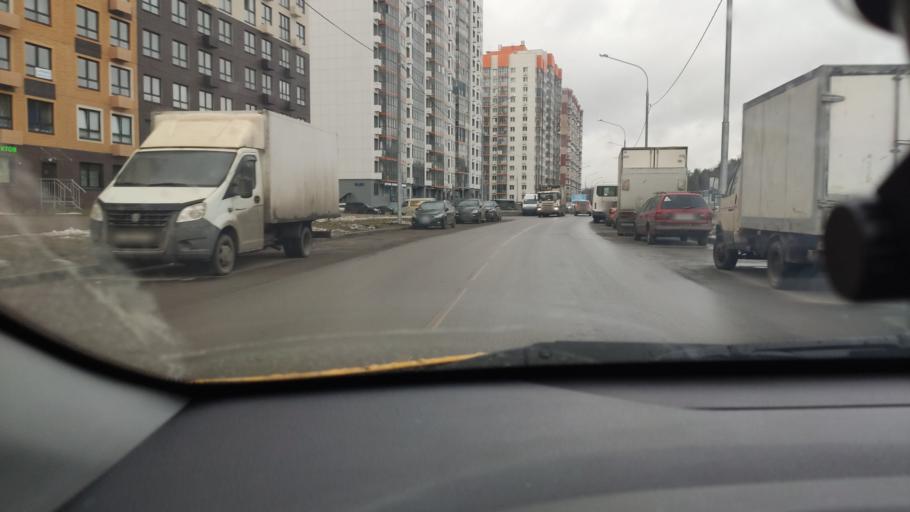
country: RU
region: Moscow
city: Annino
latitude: 55.5309
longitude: 37.6210
